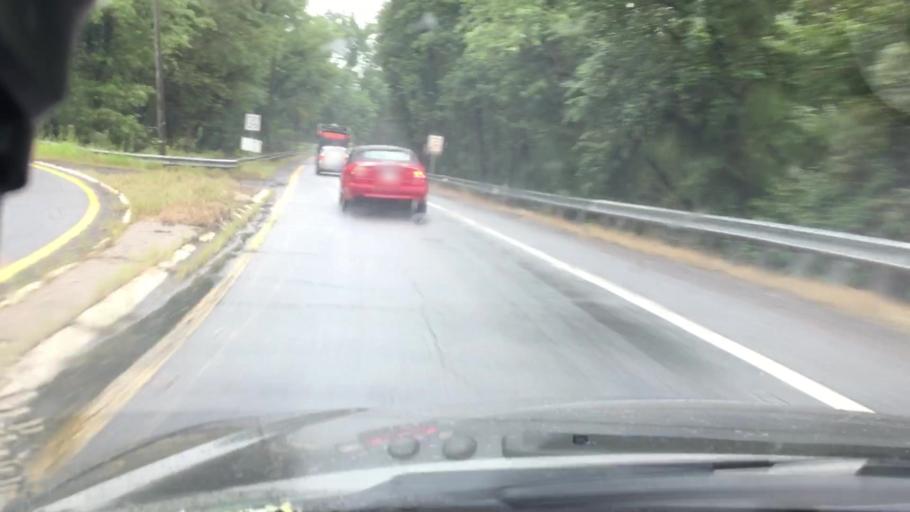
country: US
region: Pennsylvania
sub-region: Luzerne County
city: Nanticoke
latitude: 41.2182
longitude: -75.9903
